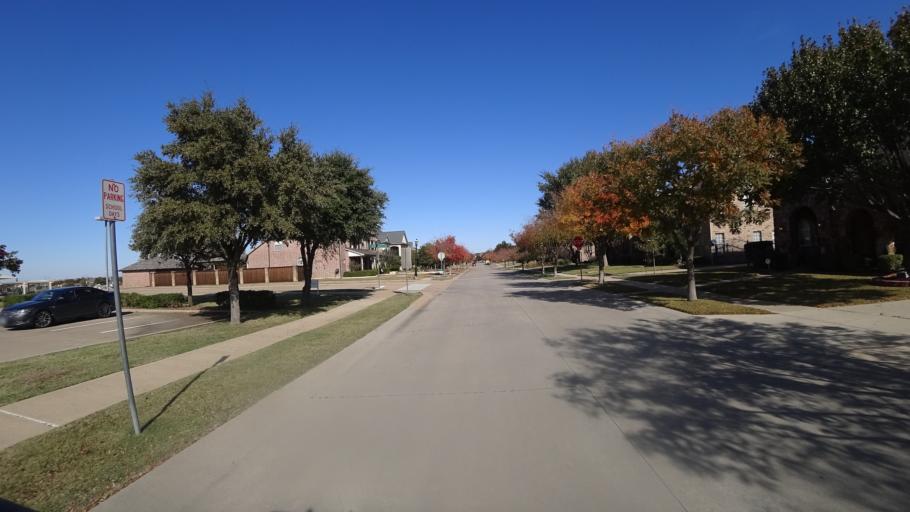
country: US
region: Texas
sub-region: Denton County
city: The Colony
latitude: 33.0315
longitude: -96.8951
